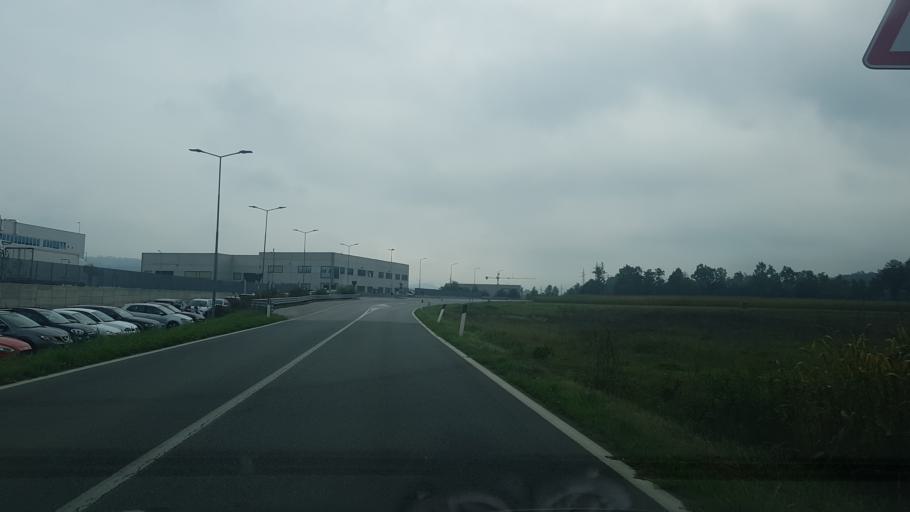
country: IT
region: Piedmont
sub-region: Provincia di Cuneo
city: Lesegno
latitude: 44.3973
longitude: 7.9883
